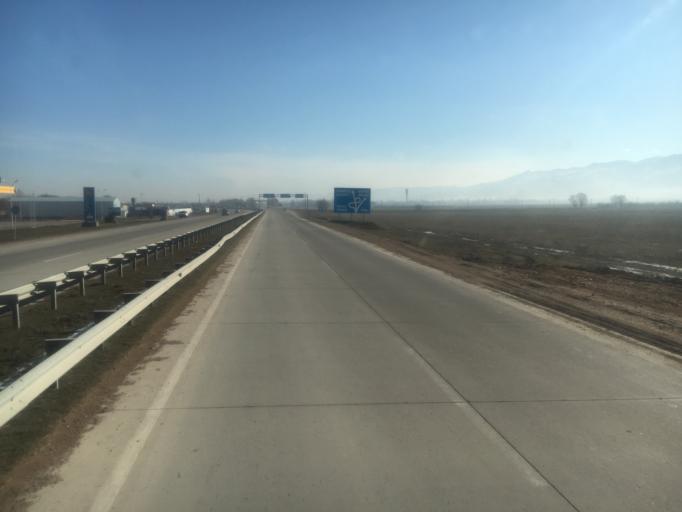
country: KZ
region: Zhambyl
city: Merke
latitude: 42.8750
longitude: 73.1242
